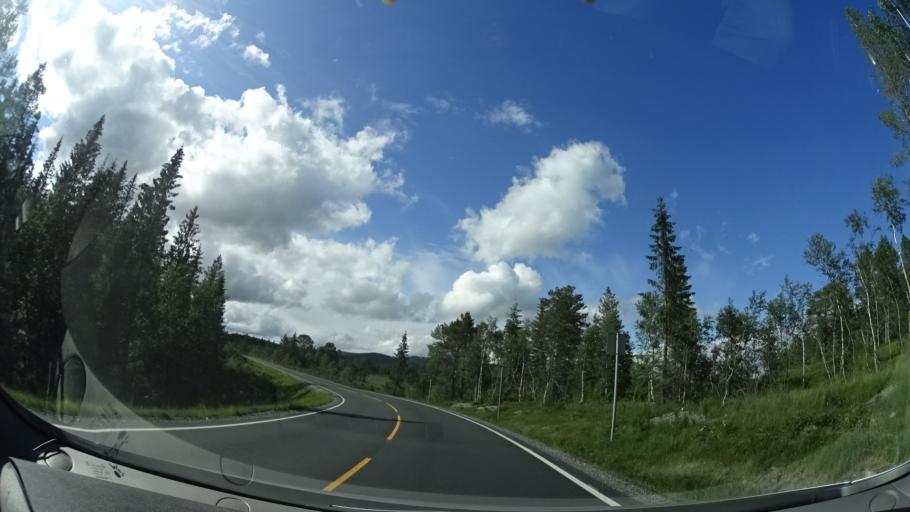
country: NO
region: Sor-Trondelag
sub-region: Snillfjord
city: Krokstadora
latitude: 63.2331
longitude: 9.5601
